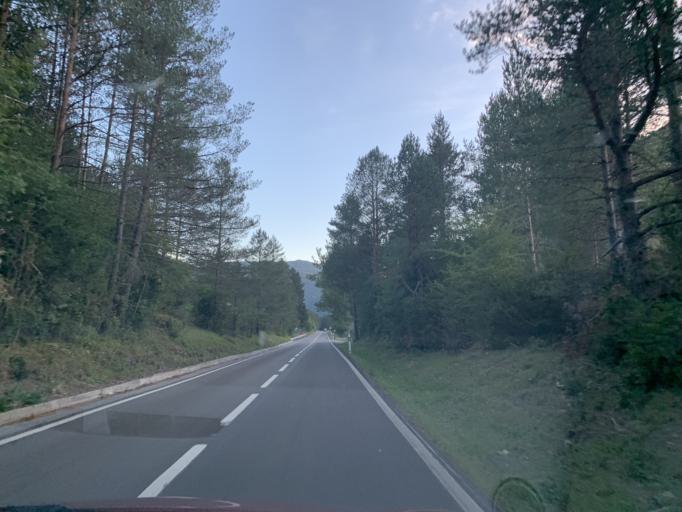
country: ES
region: Aragon
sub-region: Provincia de Huesca
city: Broto
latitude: 42.5595
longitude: -0.1175
